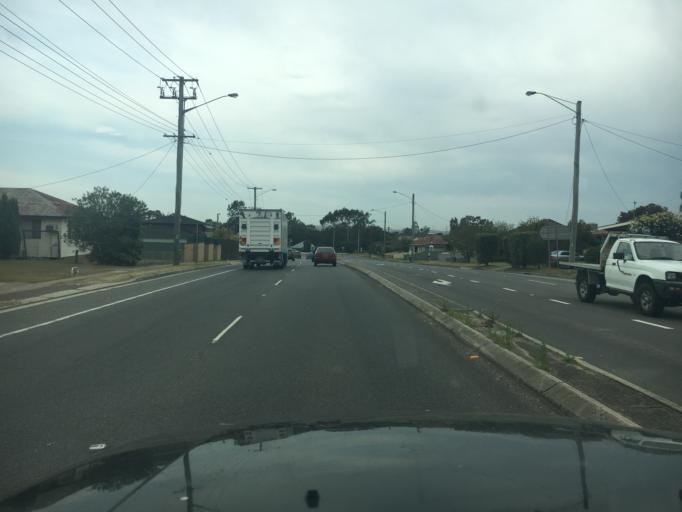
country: AU
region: New South Wales
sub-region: Maitland Municipality
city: Rutherford
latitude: -32.7179
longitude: 151.5268
